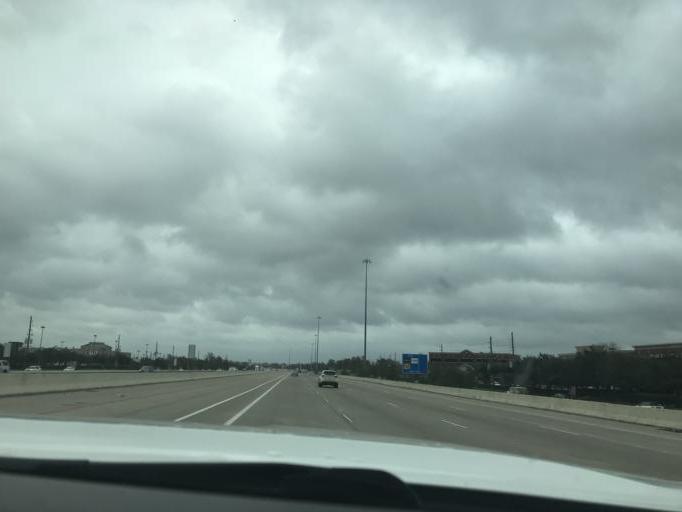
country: US
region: Texas
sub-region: Fort Bend County
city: Greatwood
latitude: 29.5623
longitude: -95.6852
